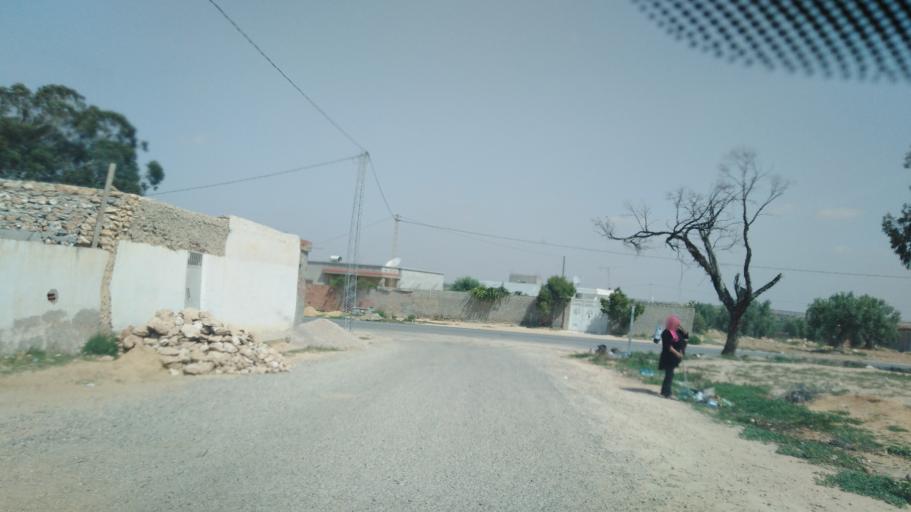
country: TN
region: Safaqis
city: Sfax
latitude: 34.7298
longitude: 10.5718
